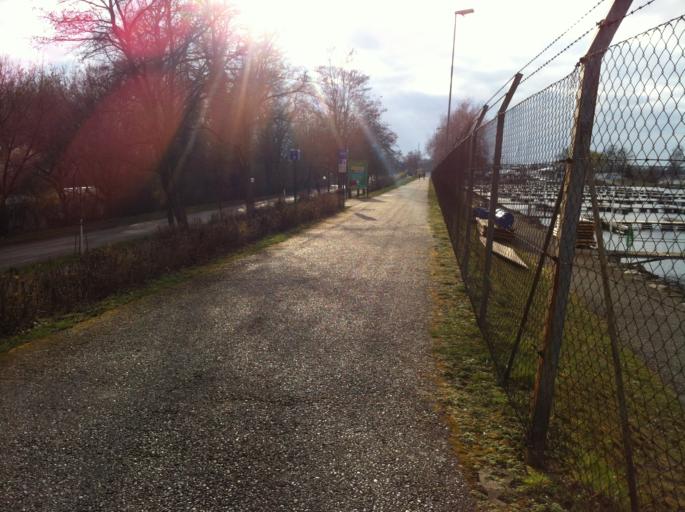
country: AT
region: Lower Austria
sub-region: Politischer Bezirk Tulln
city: Tulln
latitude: 48.3334
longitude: 16.0715
